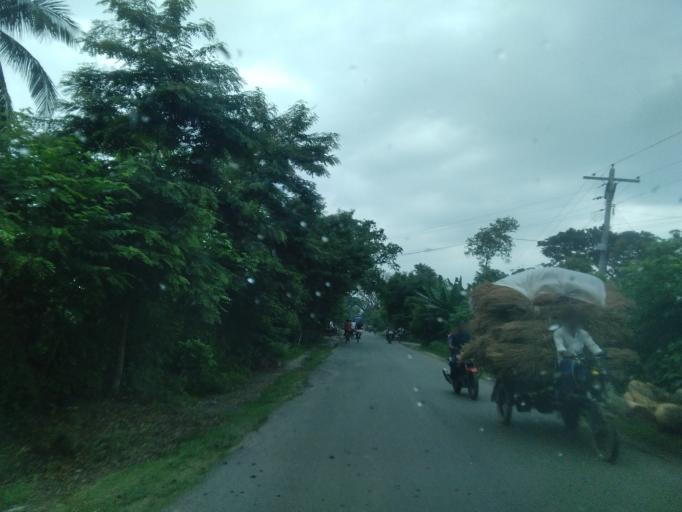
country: IN
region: West Bengal
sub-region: North 24 Parganas
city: Taki
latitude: 22.5054
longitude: 89.0128
